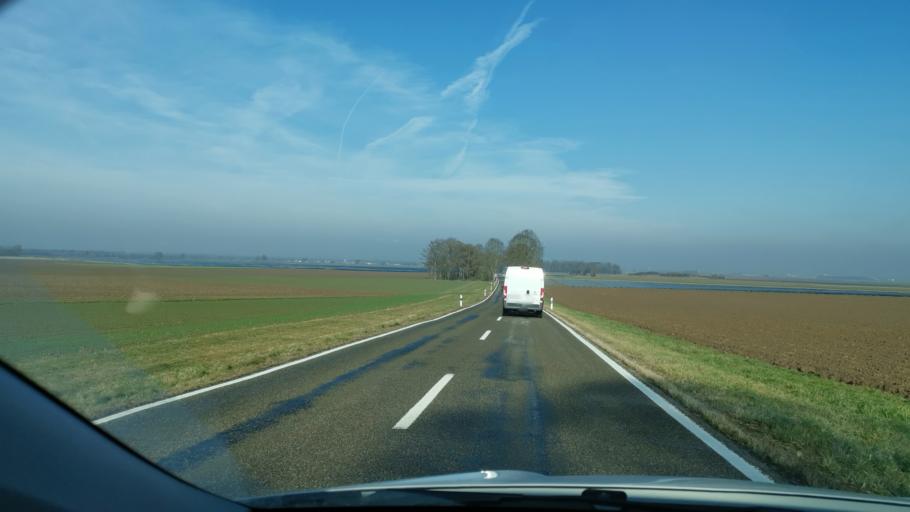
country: DE
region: Bavaria
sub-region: Swabia
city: Holzheim
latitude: 48.6286
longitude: 10.9283
